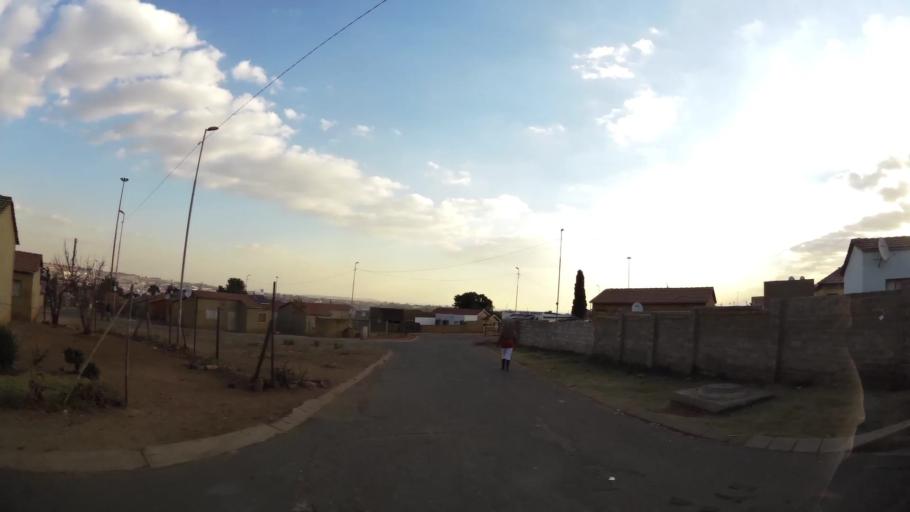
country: ZA
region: Gauteng
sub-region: West Rand District Municipality
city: Krugersdorp
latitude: -26.0794
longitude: 27.7591
